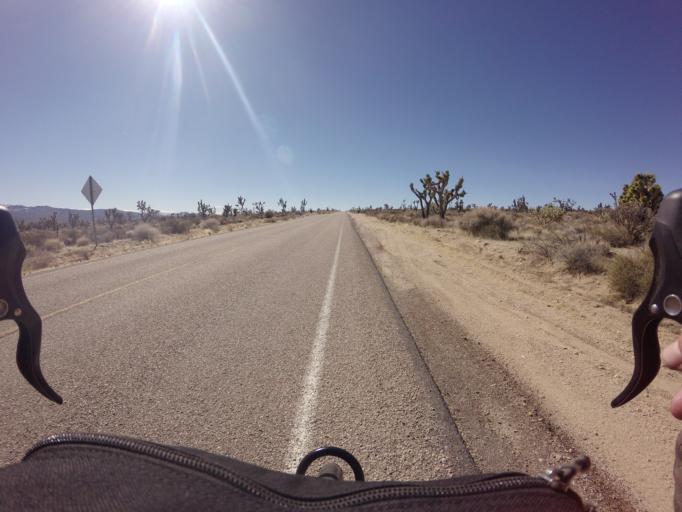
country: US
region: Nevada
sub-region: Clark County
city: Sandy Valley
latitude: 35.2913
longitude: -115.4950
